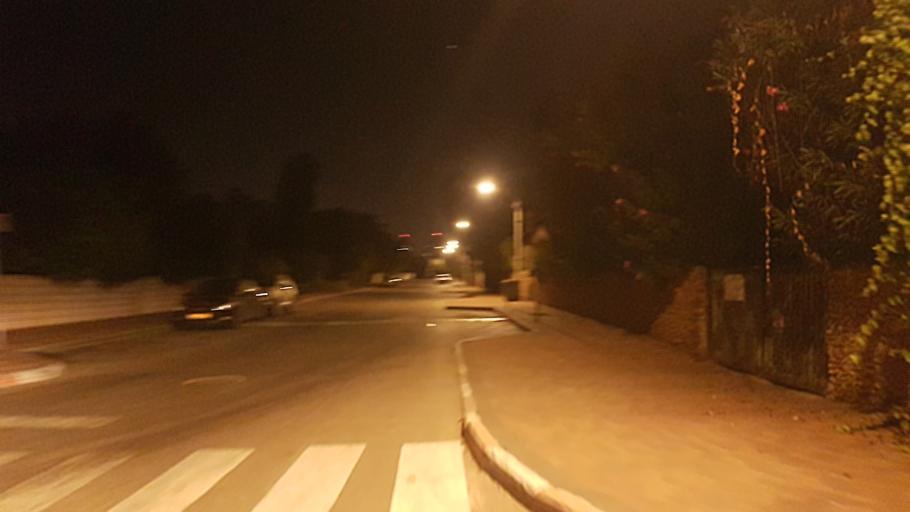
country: IL
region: Central District
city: Hod HaSharon
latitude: 32.1480
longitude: 34.9002
